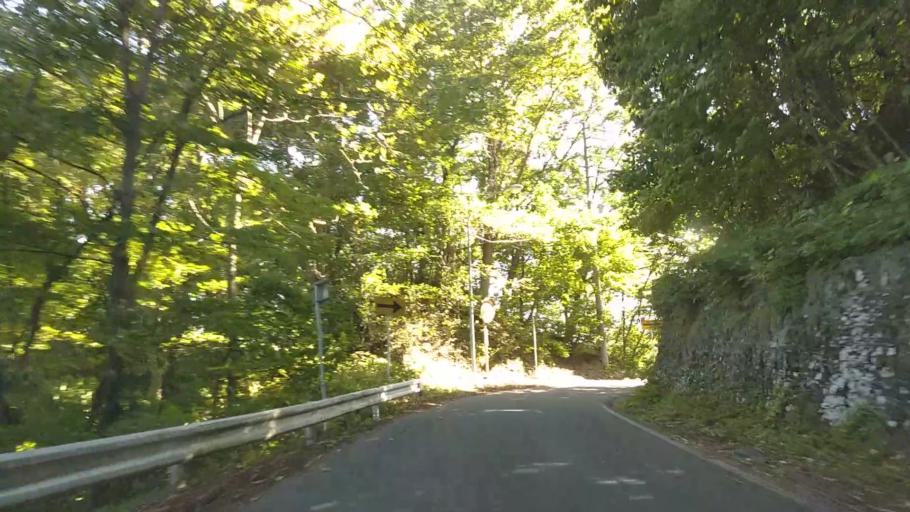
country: JP
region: Nagano
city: Nagano-shi
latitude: 36.5816
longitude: 138.0995
